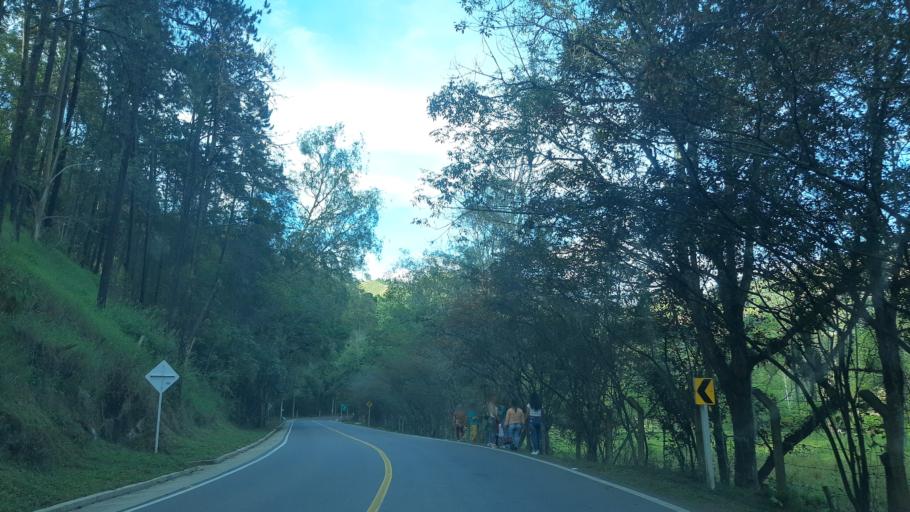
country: CO
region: Cundinamarca
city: Macheta
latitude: 5.0731
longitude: -73.5876
